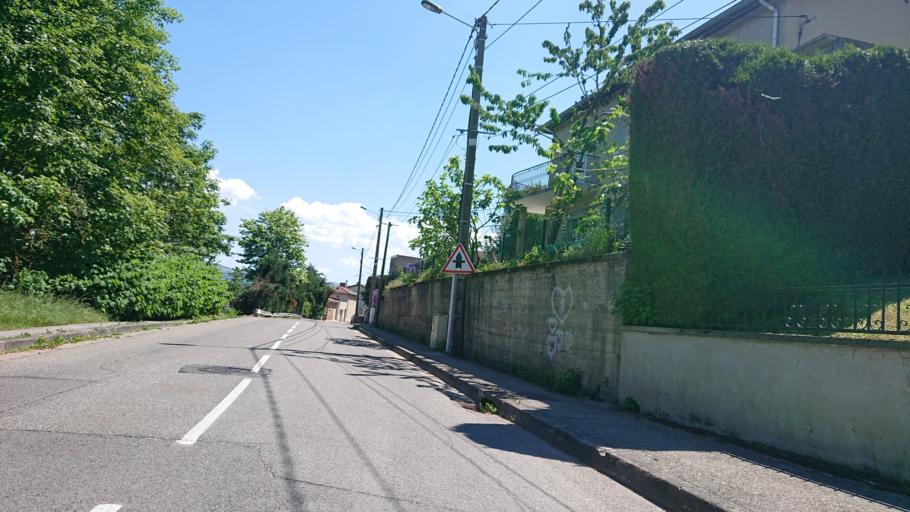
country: FR
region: Rhone-Alpes
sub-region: Departement de la Loire
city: Villars
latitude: 45.4507
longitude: 4.3602
